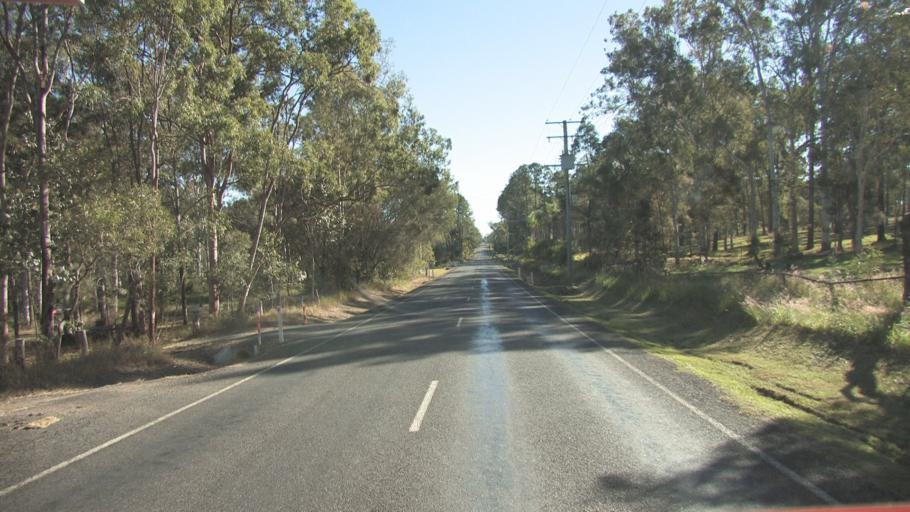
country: AU
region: Queensland
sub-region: Logan
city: Park Ridge South
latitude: -27.7230
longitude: 153.0039
